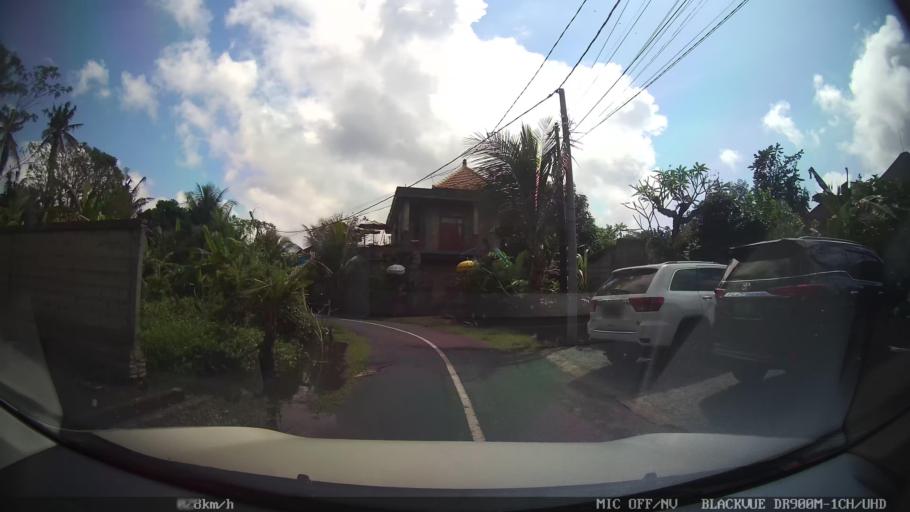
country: ID
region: Bali
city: Banjar Tebongkang
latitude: -8.5482
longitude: 115.2753
